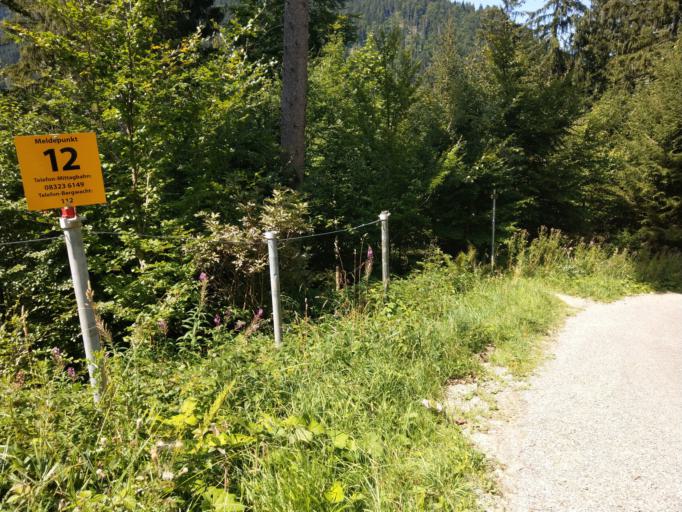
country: DE
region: Bavaria
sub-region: Swabia
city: Immenstadt im Allgau
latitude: 47.5474
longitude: 10.2145
